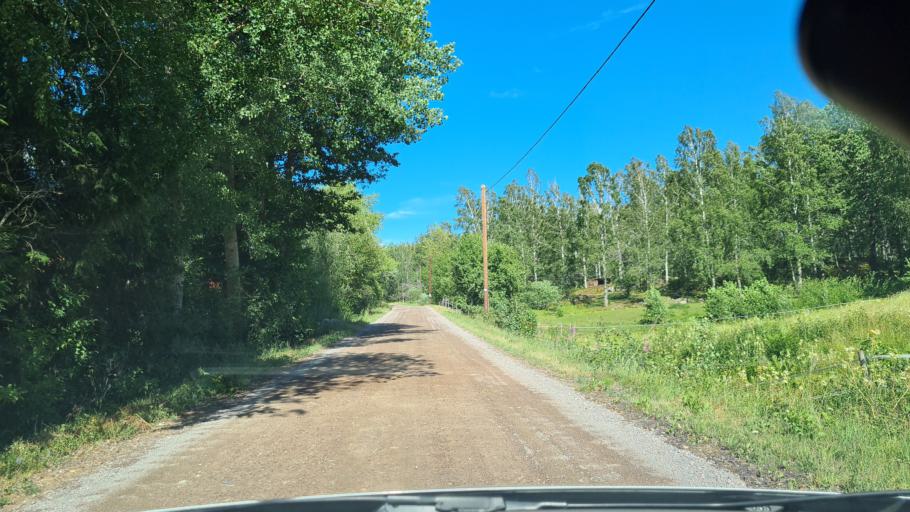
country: SE
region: OEstergoetland
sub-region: Norrkopings Kommun
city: Krokek
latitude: 58.6757
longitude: 16.4258
